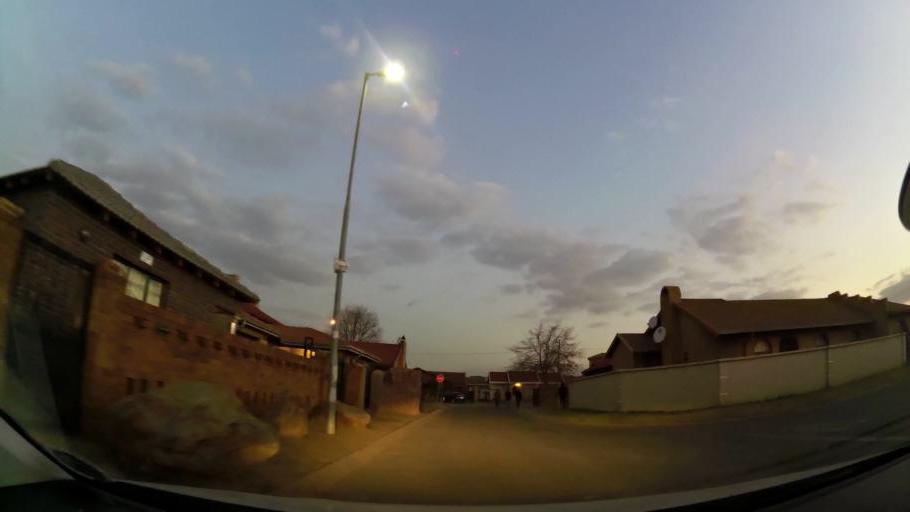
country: ZA
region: Gauteng
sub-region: City of Johannesburg Metropolitan Municipality
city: Soweto
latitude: -26.2698
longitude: 27.9057
